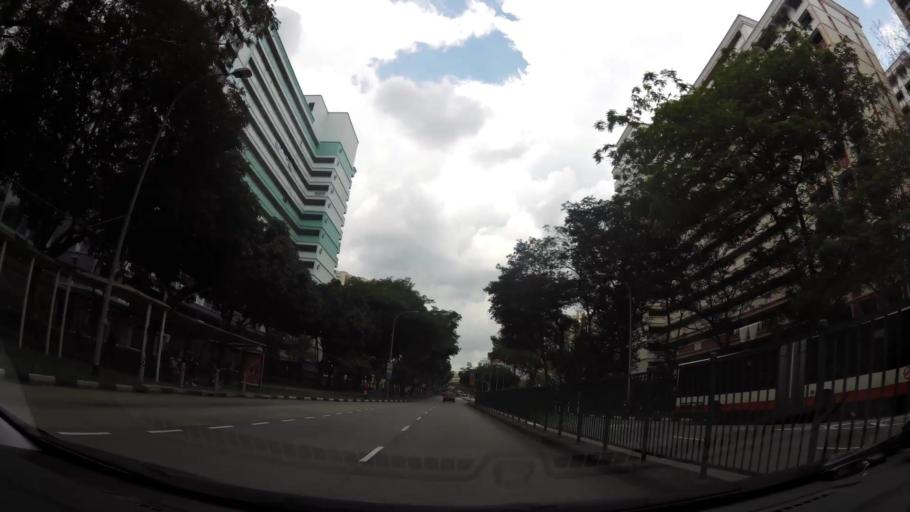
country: MY
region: Johor
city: Kampung Pasir Gudang Baru
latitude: 1.4459
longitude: 103.8198
